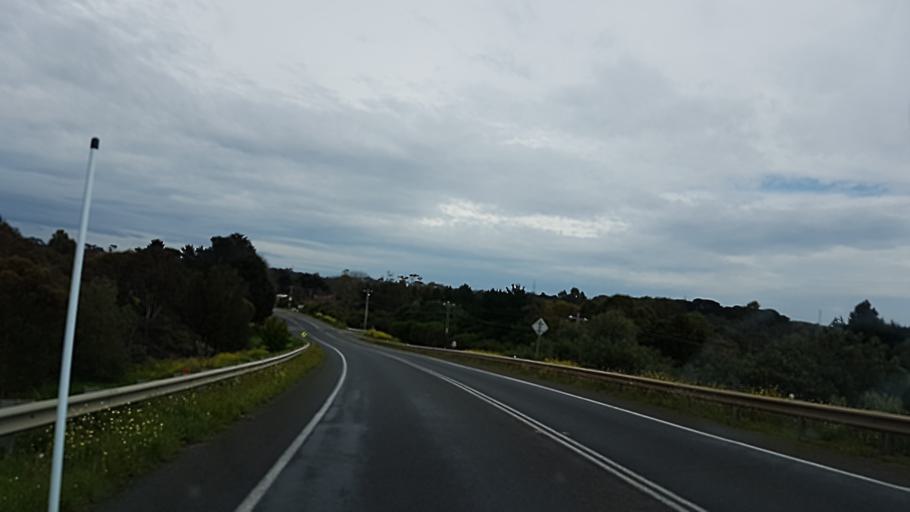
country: AU
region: Victoria
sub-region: Greater Geelong
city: Bell Post Hill
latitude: -38.0902
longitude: 144.2839
